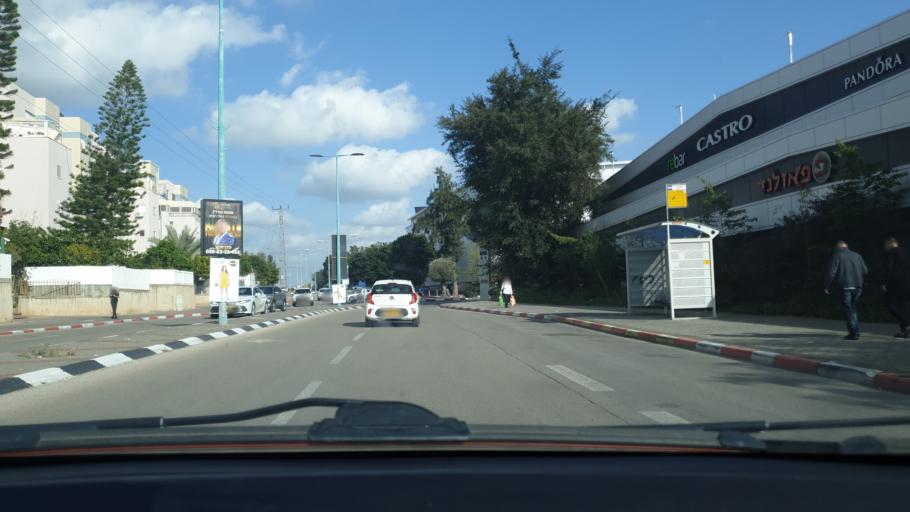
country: IL
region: Central District
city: Ramla
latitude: 31.9262
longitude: 34.8637
